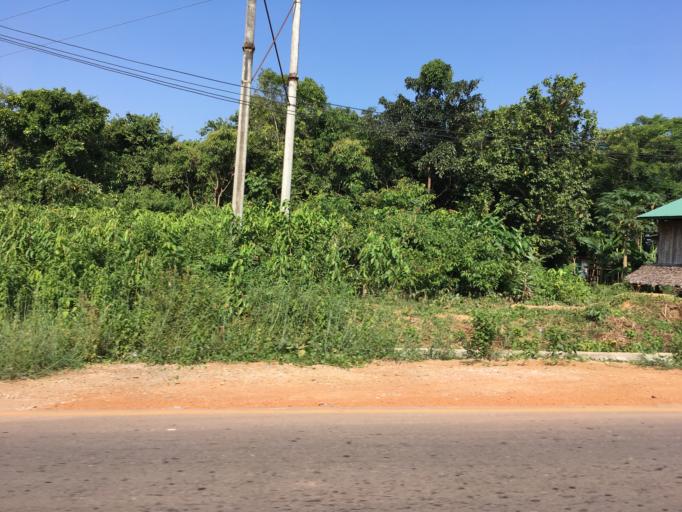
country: MM
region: Mon
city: Martaban
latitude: 16.7005
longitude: 97.7564
